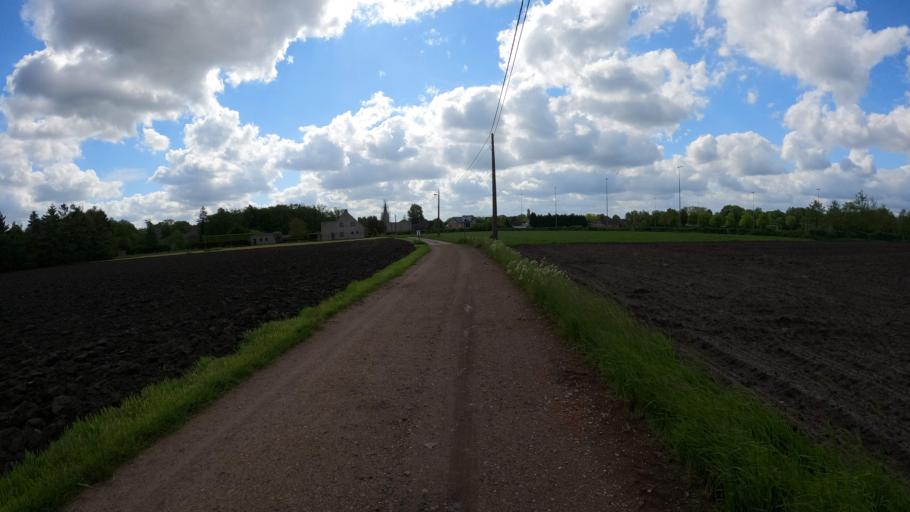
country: BE
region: Flanders
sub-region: Provincie Antwerpen
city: Zoersel
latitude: 51.3039
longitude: 4.6842
